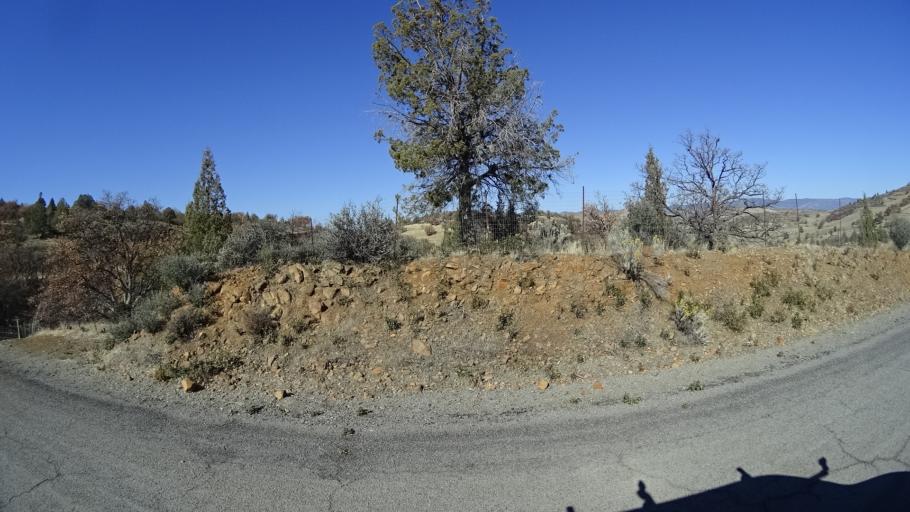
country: US
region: California
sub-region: Siskiyou County
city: Montague
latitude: 41.8789
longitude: -122.4782
